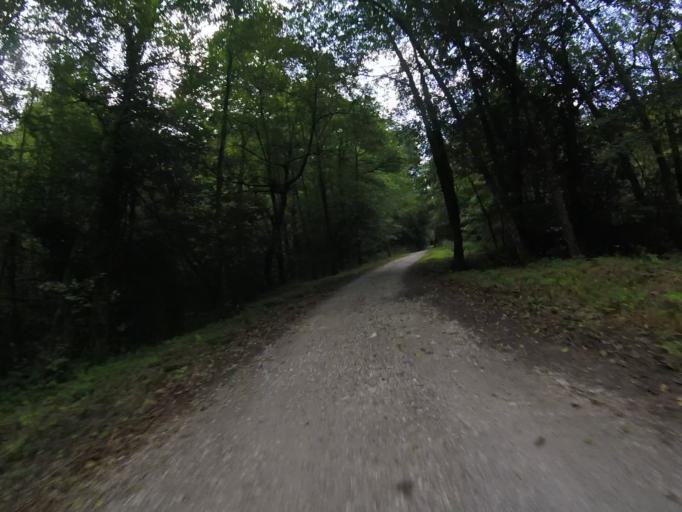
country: ES
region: Basque Country
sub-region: Provincia de Guipuzcoa
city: Elduayen
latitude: 43.1746
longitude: -1.9647
